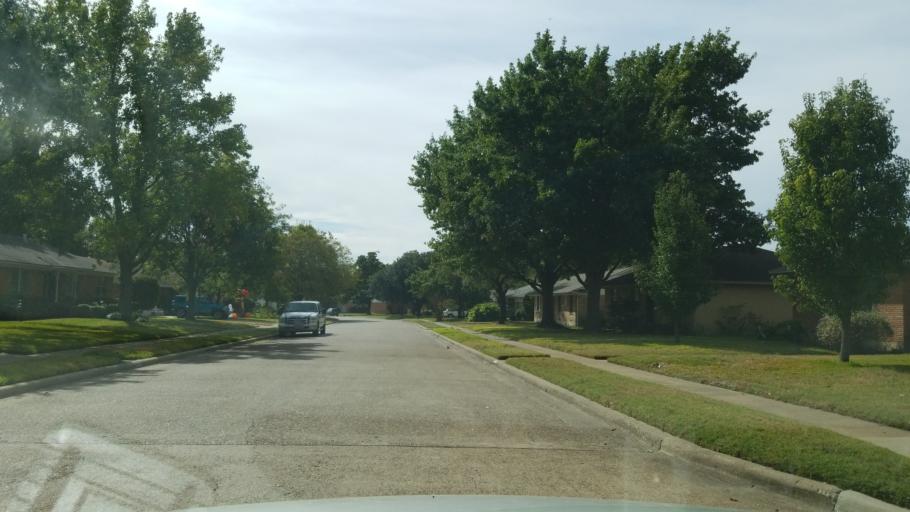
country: US
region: Texas
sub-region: Dallas County
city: Garland
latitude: 32.9019
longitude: -96.6640
